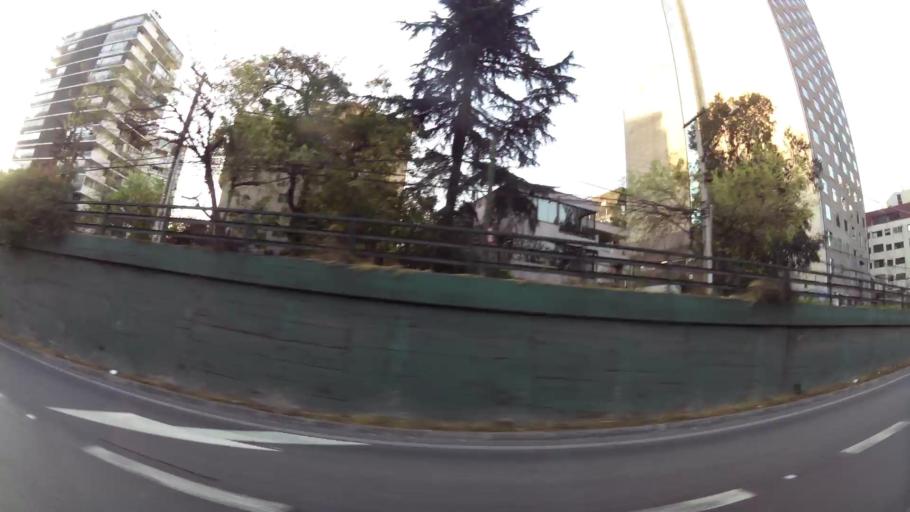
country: CL
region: Santiago Metropolitan
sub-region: Provincia de Santiago
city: Villa Presidente Frei, Nunoa, Santiago, Chile
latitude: -33.4080
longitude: -70.5989
